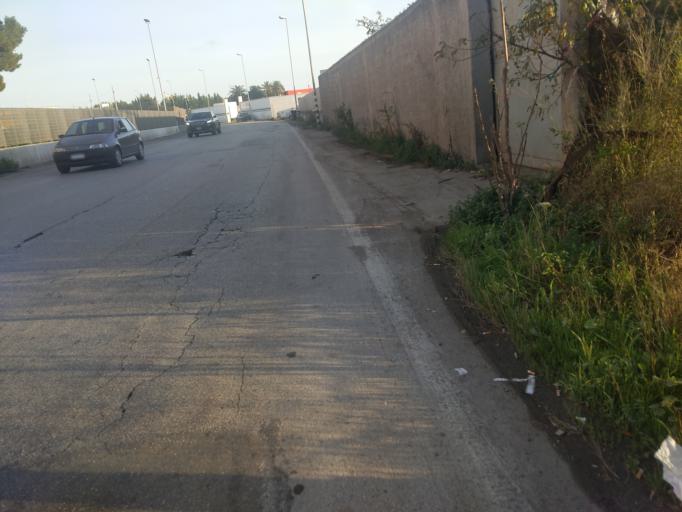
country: IT
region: Apulia
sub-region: Provincia di Bari
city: Bari
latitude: 41.1152
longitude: 16.8380
